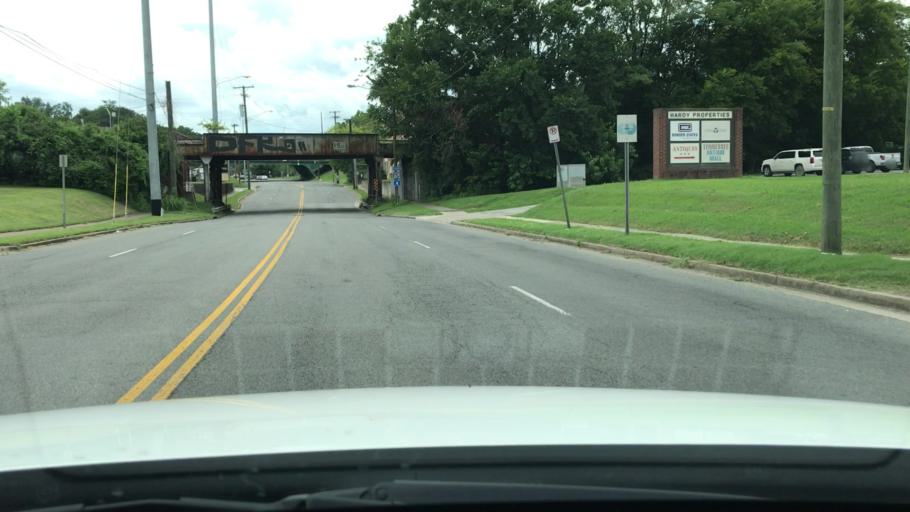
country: US
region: Tennessee
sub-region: Davidson County
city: Nashville
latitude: 36.1341
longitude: -86.7724
